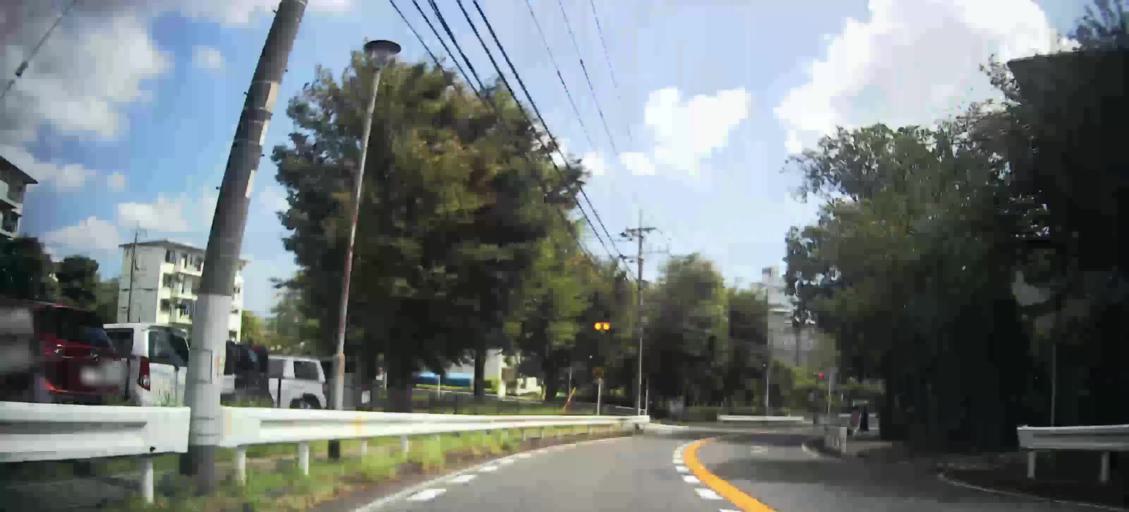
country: JP
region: Kanagawa
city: Yokohama
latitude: 35.4586
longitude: 139.5524
